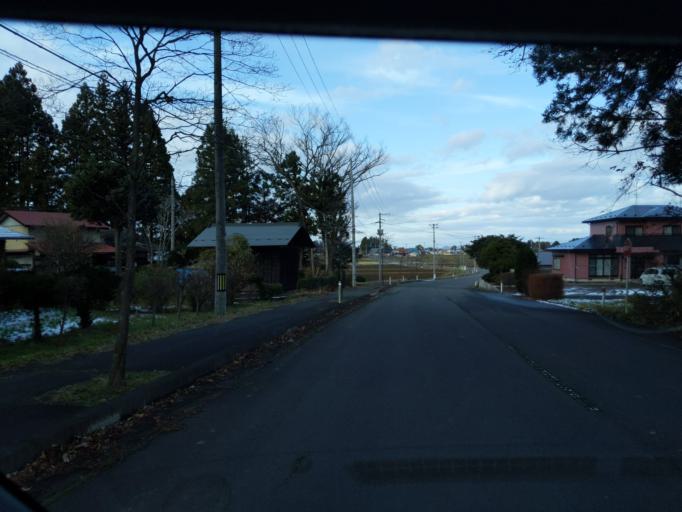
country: JP
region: Iwate
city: Mizusawa
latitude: 39.1181
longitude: 141.0920
